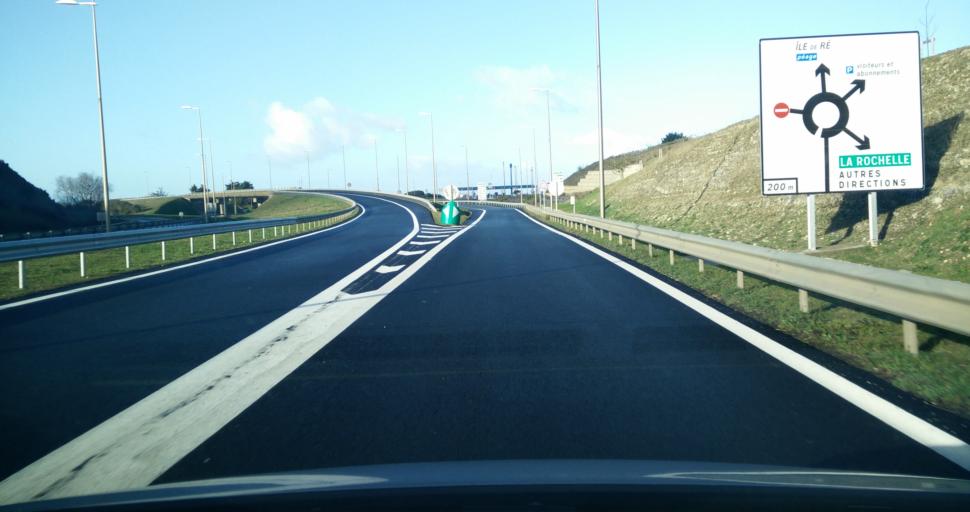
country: FR
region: Poitou-Charentes
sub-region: Departement de la Charente-Maritime
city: Nieul-sur-Mer
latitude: 46.1756
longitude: -1.2127
